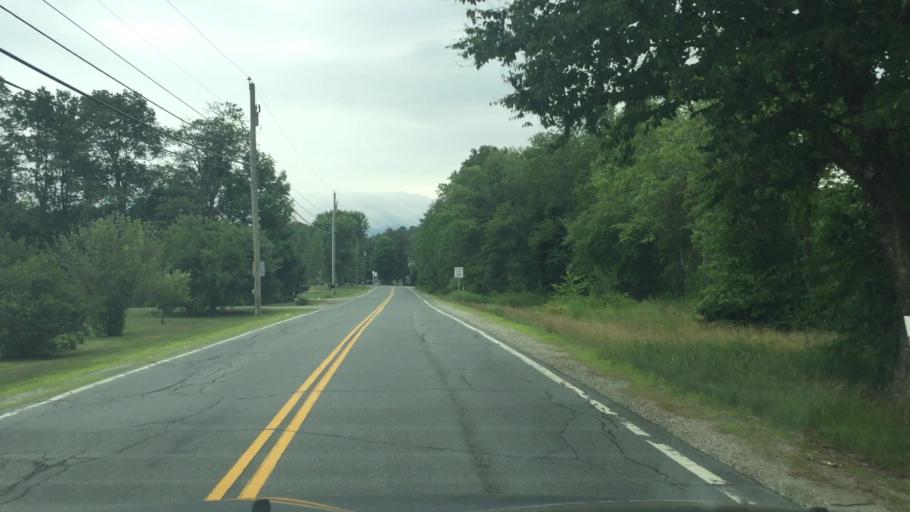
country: US
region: New Hampshire
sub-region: Grafton County
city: Littleton
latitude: 44.2364
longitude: -71.7581
